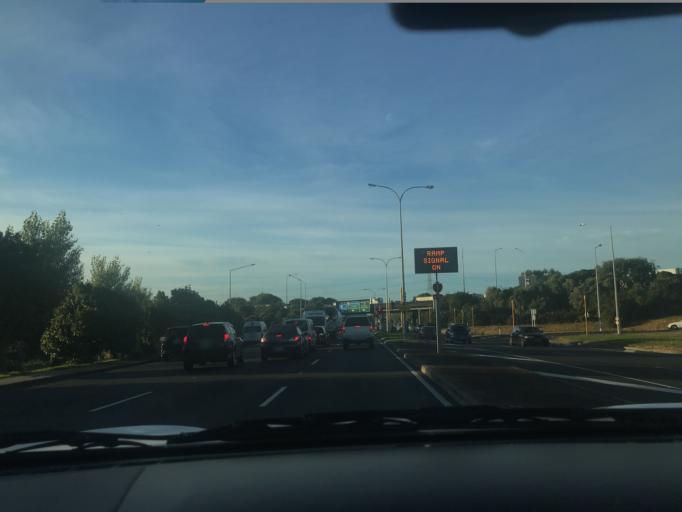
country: NZ
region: Auckland
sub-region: Auckland
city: Tamaki
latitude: -36.9173
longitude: 174.8396
